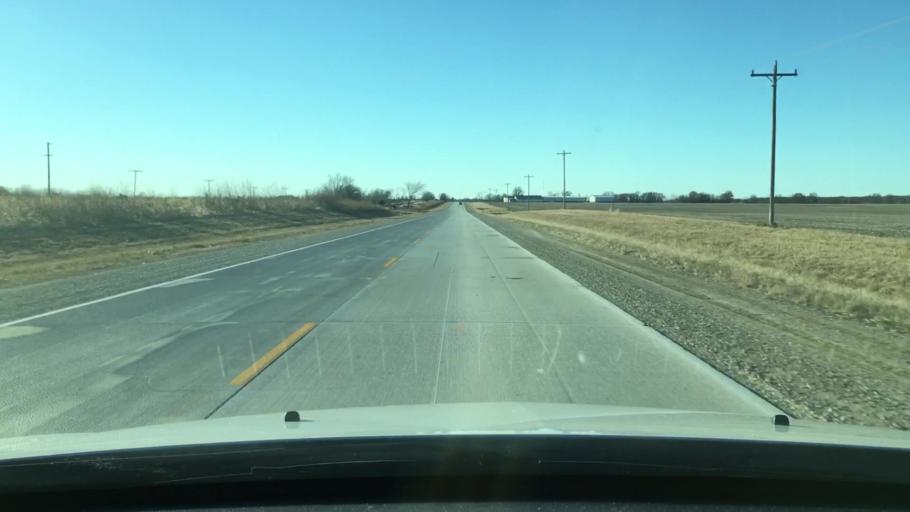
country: US
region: Missouri
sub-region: Boone County
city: Centralia
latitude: 39.2001
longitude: -92.0538
